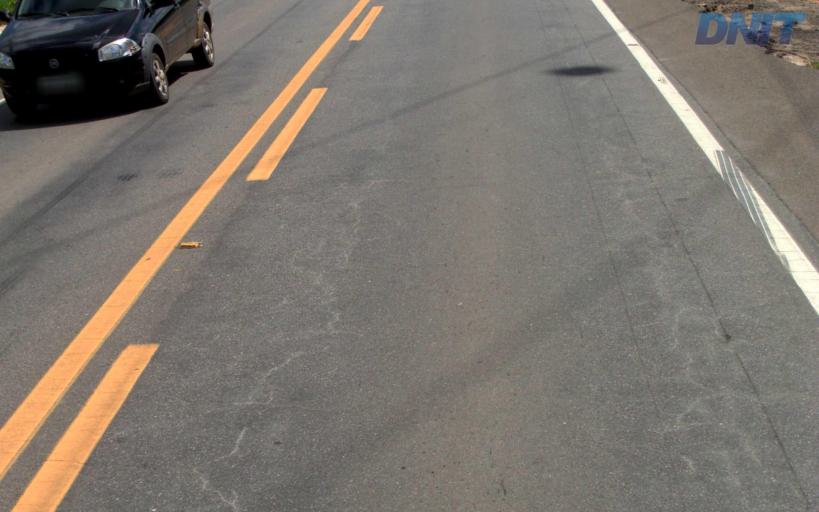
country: BR
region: Minas Gerais
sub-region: Belo Oriente
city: Belo Oriente
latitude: -19.0881
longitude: -42.1883
